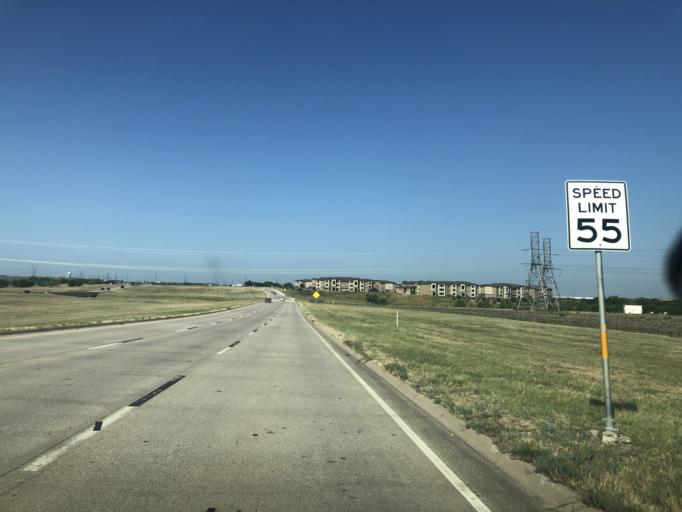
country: US
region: Texas
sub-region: Tarrant County
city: Keller
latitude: 32.9688
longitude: -97.2897
